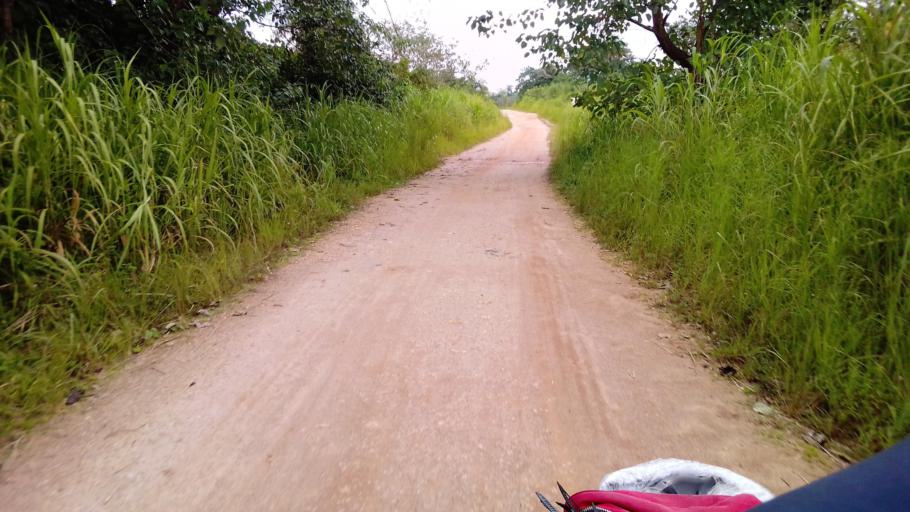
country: SL
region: Eastern Province
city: Koidu
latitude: 8.6807
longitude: -10.9748
